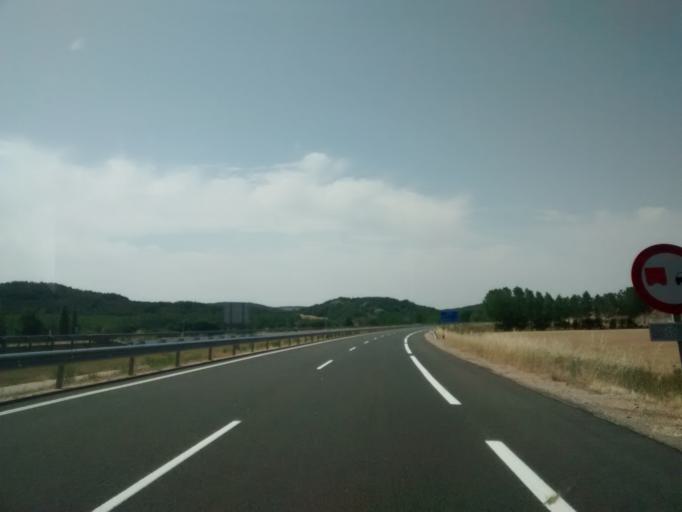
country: ES
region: Castille and Leon
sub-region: Provincia de Palencia
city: Alar del Rey
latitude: 42.7105
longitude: -4.2883
